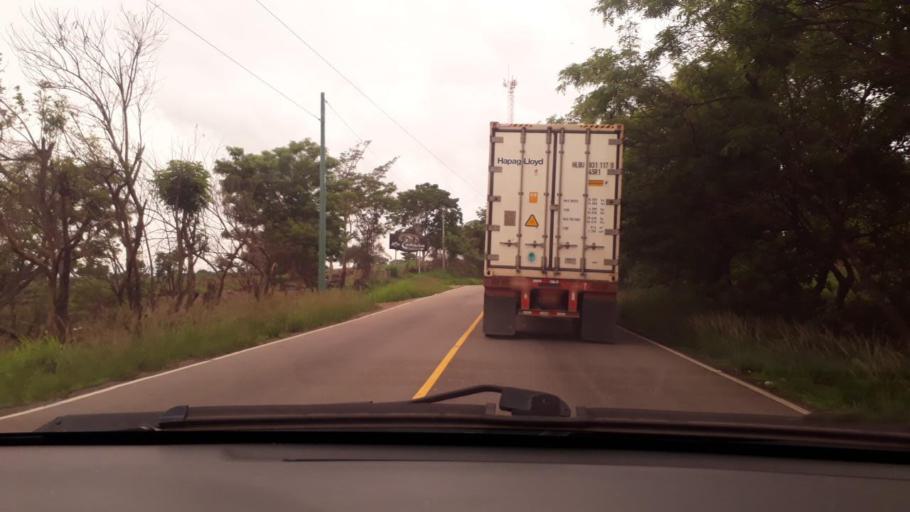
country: GT
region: Chiquimula
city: Quezaltepeque
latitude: 14.5863
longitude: -89.4554
